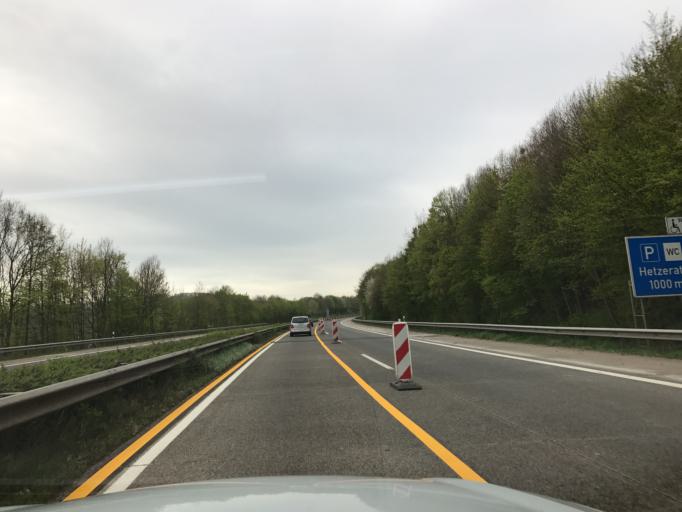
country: DE
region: Rheinland-Pfalz
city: Rivenich
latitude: 49.8814
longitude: 6.8455
